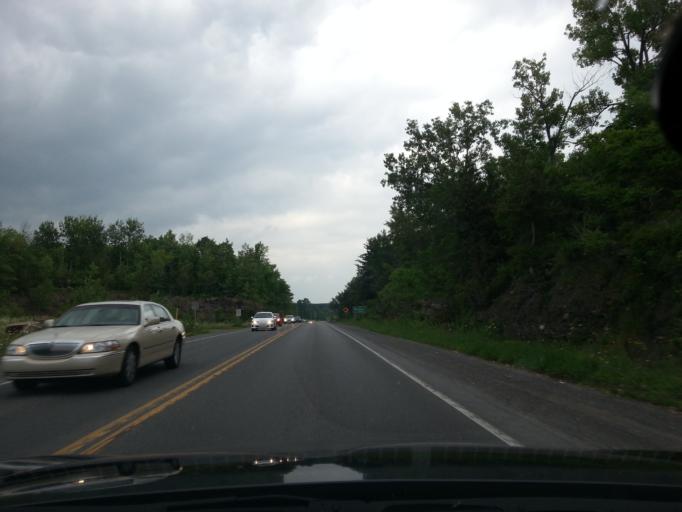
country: CA
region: Ontario
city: Clarence-Rockland
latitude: 45.5533
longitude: -75.2913
